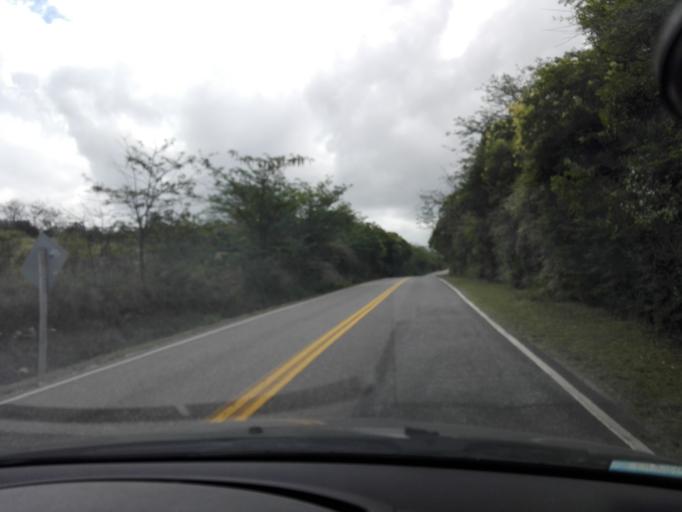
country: AR
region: Cordoba
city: Cuesta Blanca
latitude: -31.5916
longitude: -64.5745
